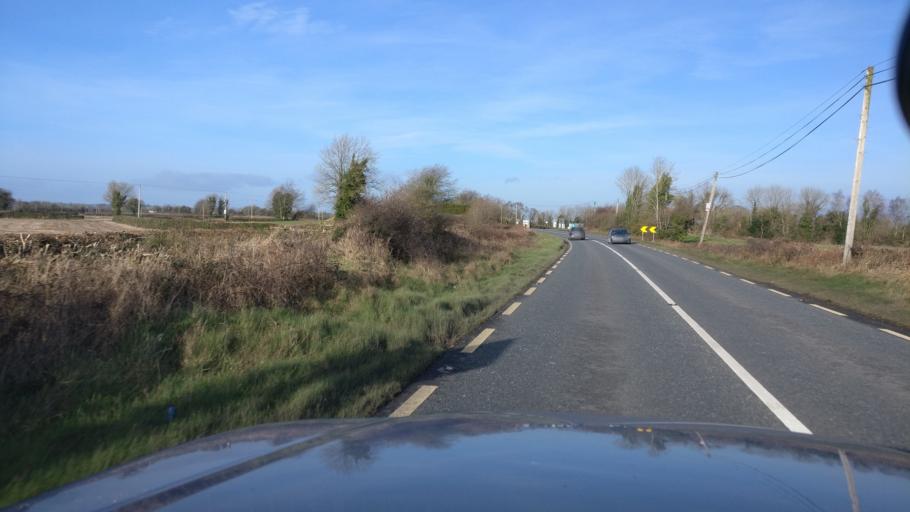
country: IE
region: Leinster
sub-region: Laois
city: Mountmellick
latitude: 53.1576
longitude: -7.3680
